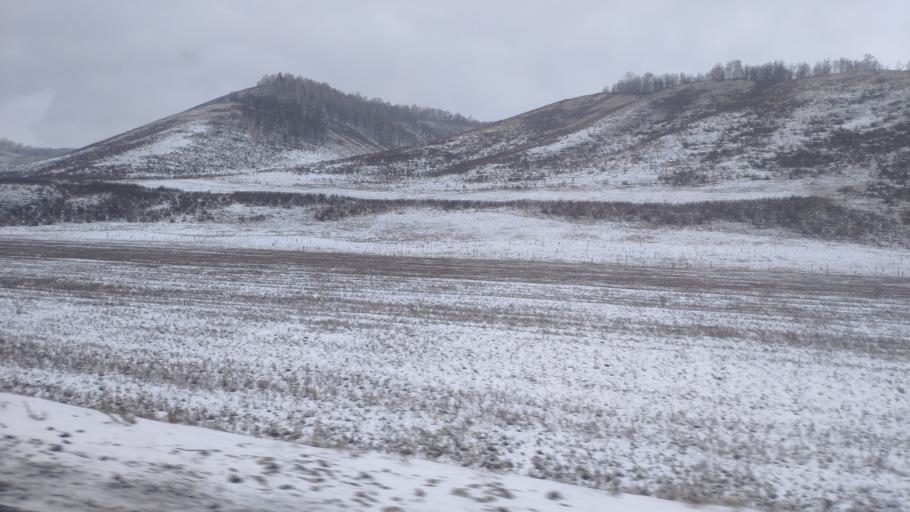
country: RU
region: Bashkortostan
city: Isyangulovo
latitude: 52.1617
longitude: 56.9027
